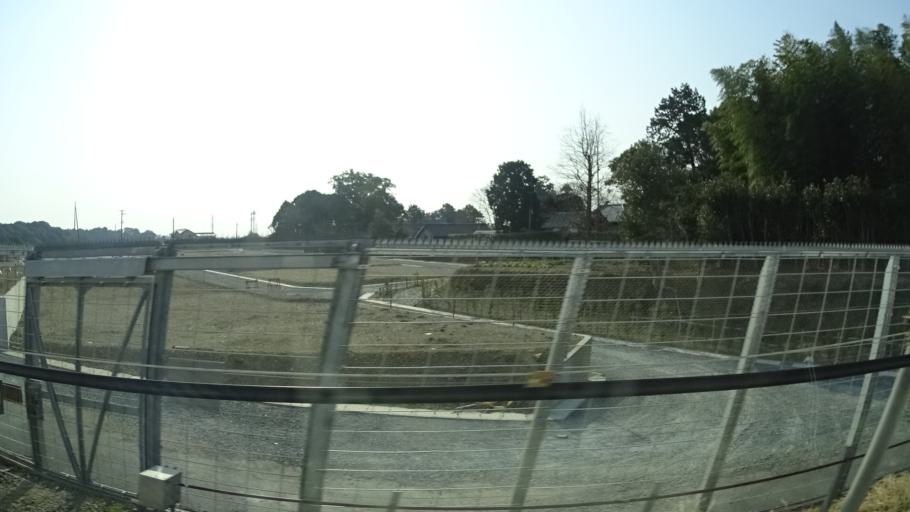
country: JP
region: Shizuoka
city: Iwata
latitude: 34.7167
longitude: 137.8839
